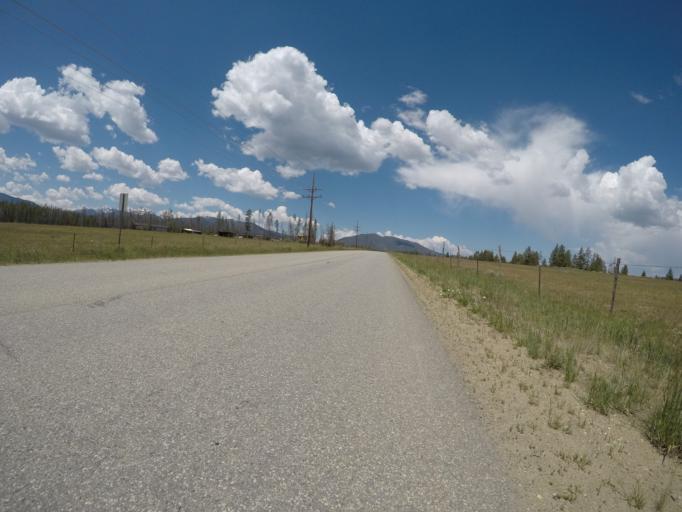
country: US
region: Colorado
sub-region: Grand County
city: Fraser
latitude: 39.9555
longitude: -105.8325
